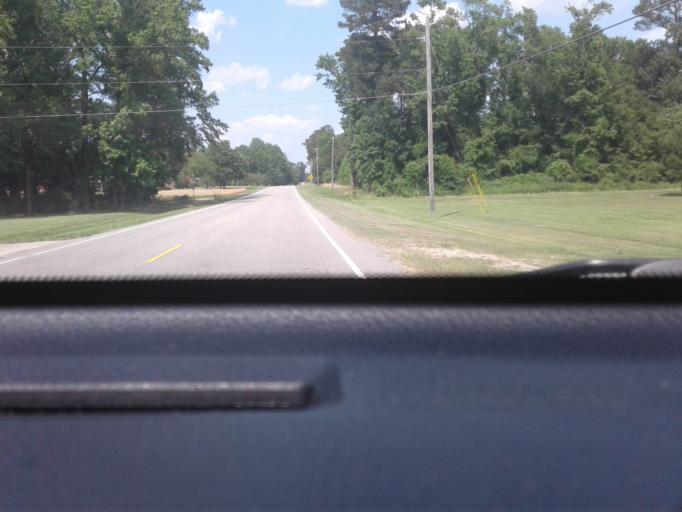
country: US
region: North Carolina
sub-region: Cumberland County
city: Eastover
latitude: 35.1317
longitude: -78.7526
